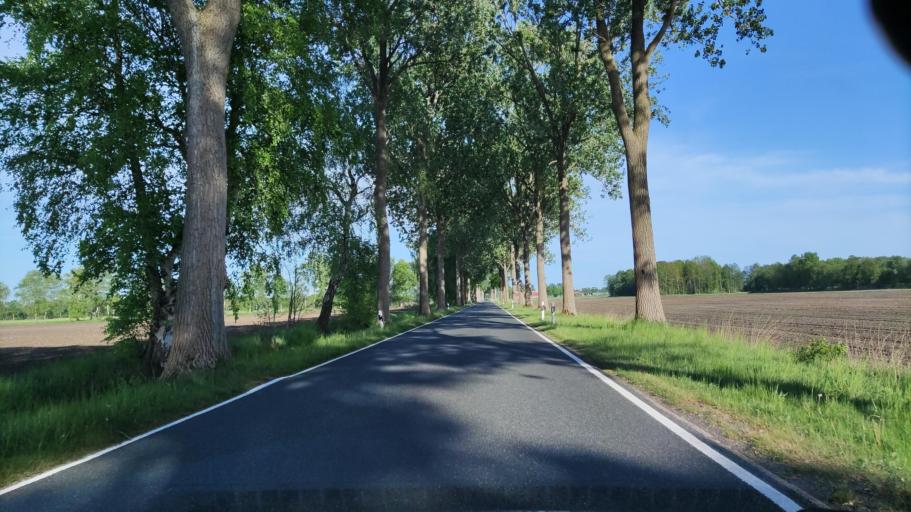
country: DE
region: Lower Saxony
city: Konigsmoor
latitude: 53.2238
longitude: 9.6964
